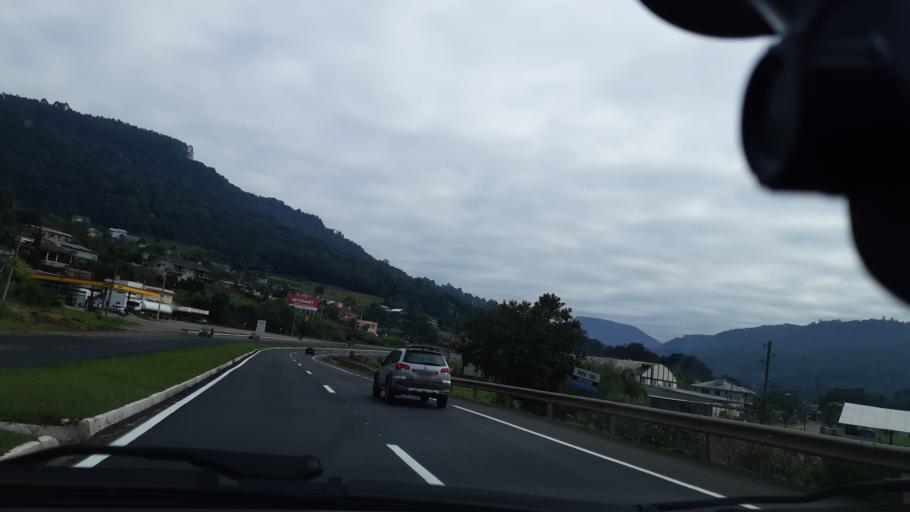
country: BR
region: Rio Grande do Sul
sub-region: Farroupilha
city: Farroupilha
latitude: -29.4005
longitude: -51.3565
